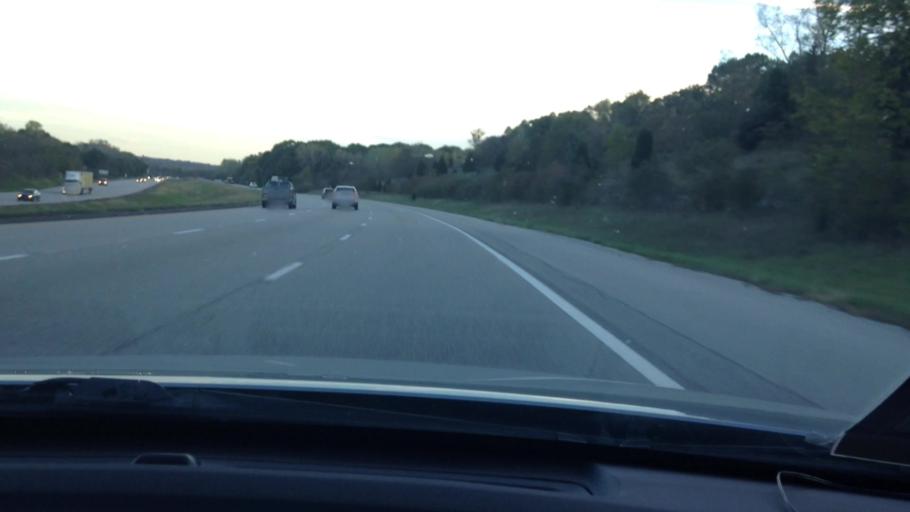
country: US
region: Missouri
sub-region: Platte County
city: Weatherby Lake
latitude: 39.2199
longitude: -94.7637
